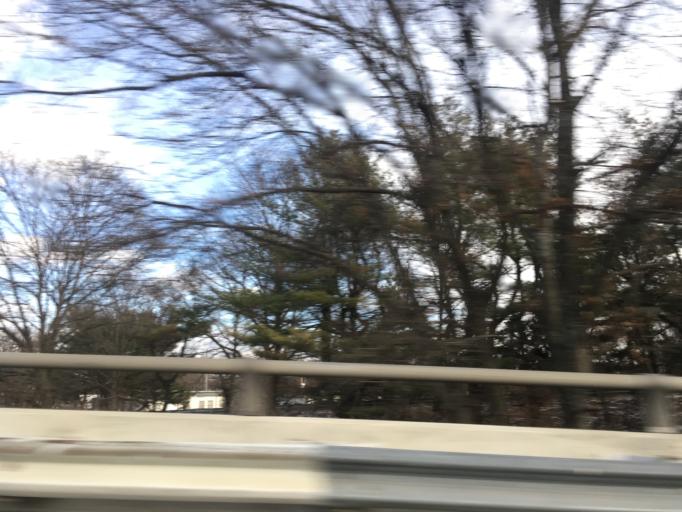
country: US
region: Rhode Island
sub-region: Providence County
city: Cranston
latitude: 41.7825
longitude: -71.4234
